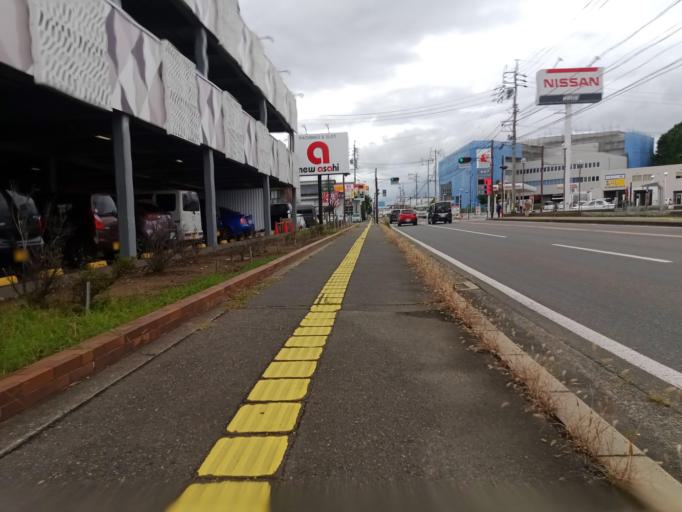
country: JP
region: Nagano
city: Nagano-shi
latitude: 36.6147
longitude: 138.1764
